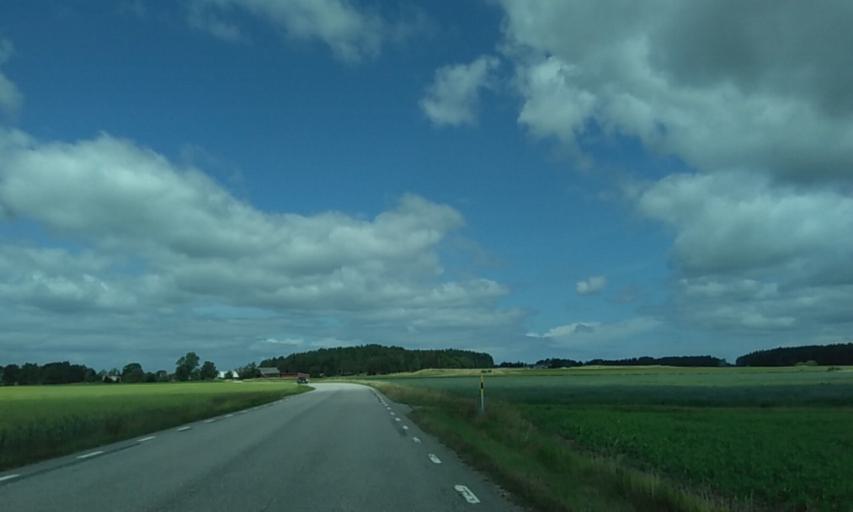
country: SE
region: Vaestra Goetaland
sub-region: Grastorps Kommun
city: Graestorp
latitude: 58.3570
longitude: 12.6789
